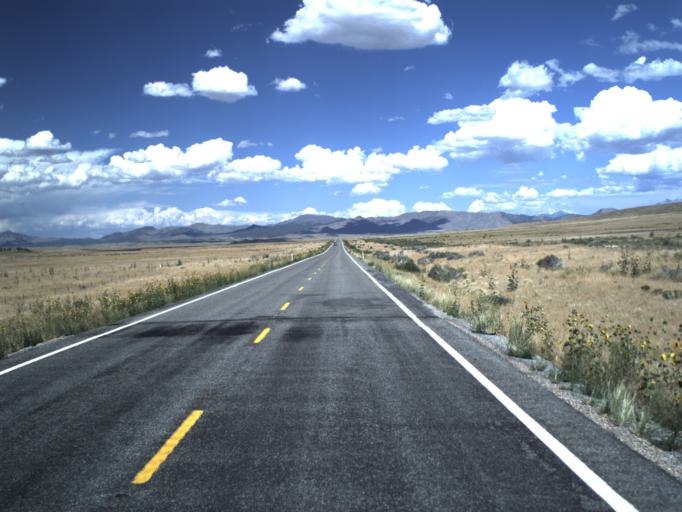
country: US
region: Utah
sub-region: Millard County
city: Delta
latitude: 39.6535
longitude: -112.2907
